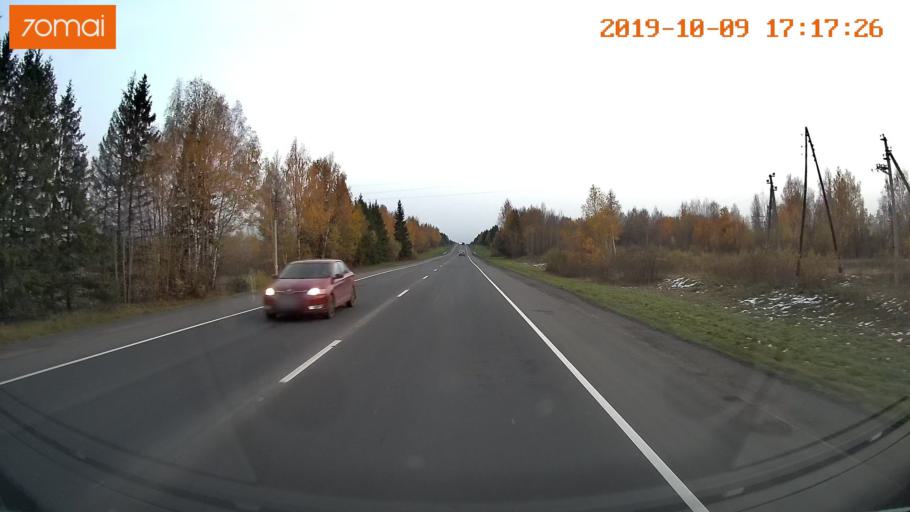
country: RU
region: Ivanovo
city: Furmanov
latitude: 57.2757
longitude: 41.1585
